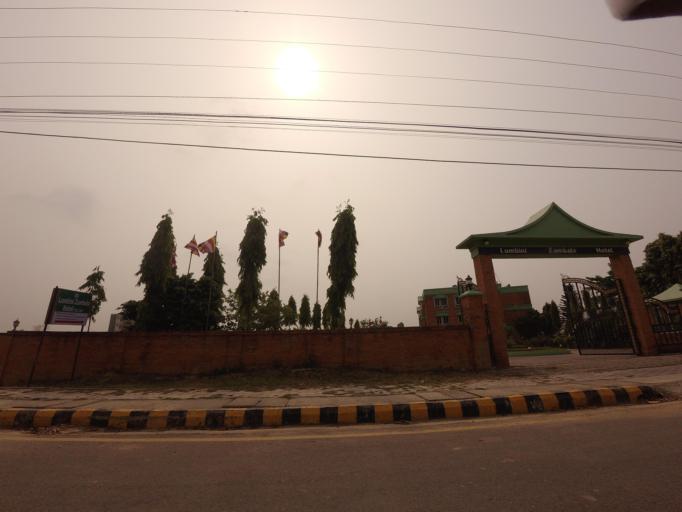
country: IN
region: Uttar Pradesh
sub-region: Maharajganj
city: Nautanwa
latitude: 27.4752
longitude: 83.2840
